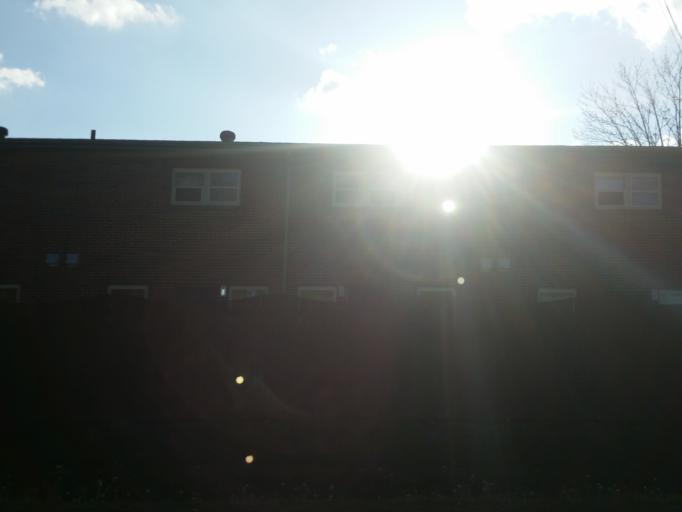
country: US
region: Kentucky
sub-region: Bell County
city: Middlesboro
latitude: 36.6020
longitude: -83.7421
